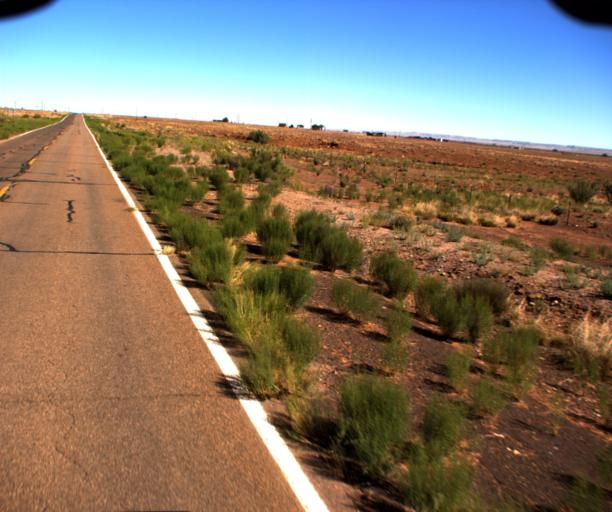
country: US
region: Arizona
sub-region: Coconino County
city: LeChee
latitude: 35.2728
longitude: -110.9766
